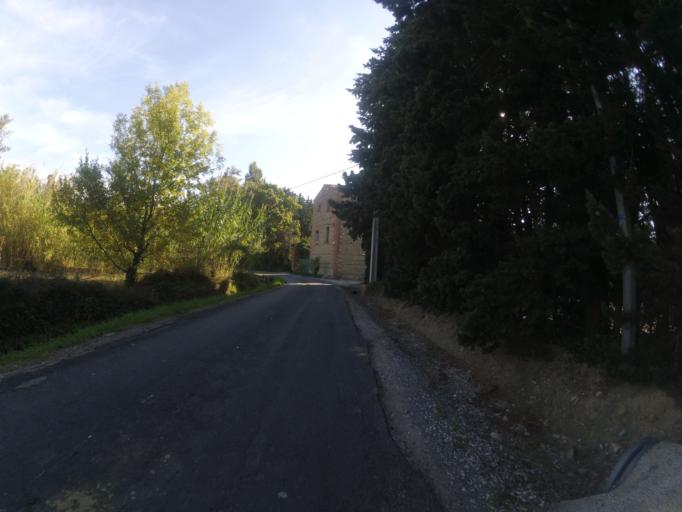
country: FR
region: Languedoc-Roussillon
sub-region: Departement des Pyrenees-Orientales
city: Pezilla-la-Riviere
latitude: 42.6929
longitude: 2.7593
